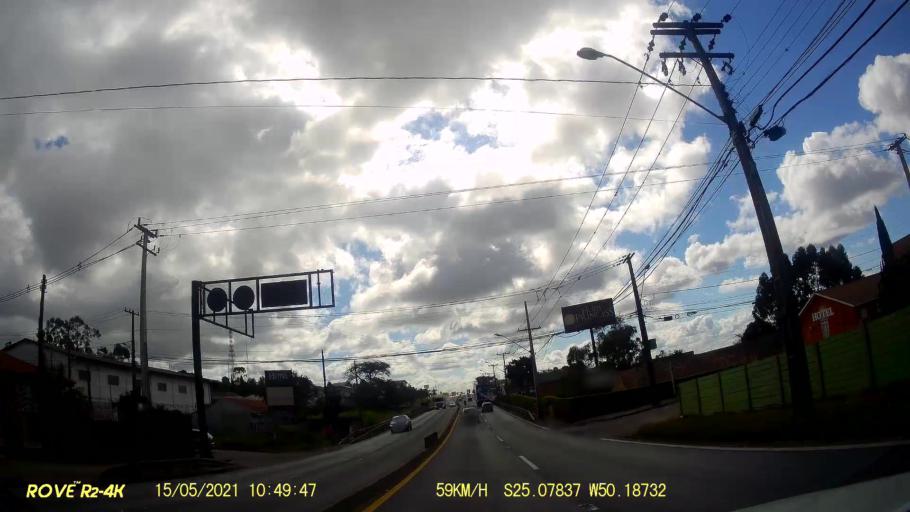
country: BR
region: Parana
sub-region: Ponta Grossa
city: Ponta Grossa
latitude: -25.0784
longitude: -50.1873
